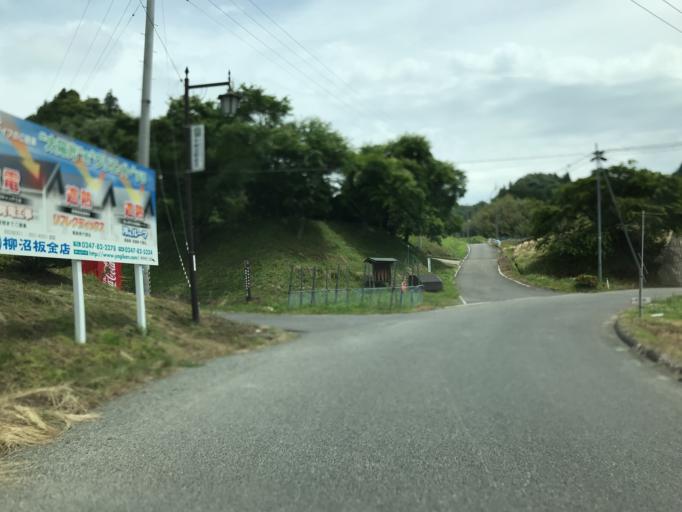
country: JP
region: Fukushima
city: Miharu
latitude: 37.4120
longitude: 140.5228
